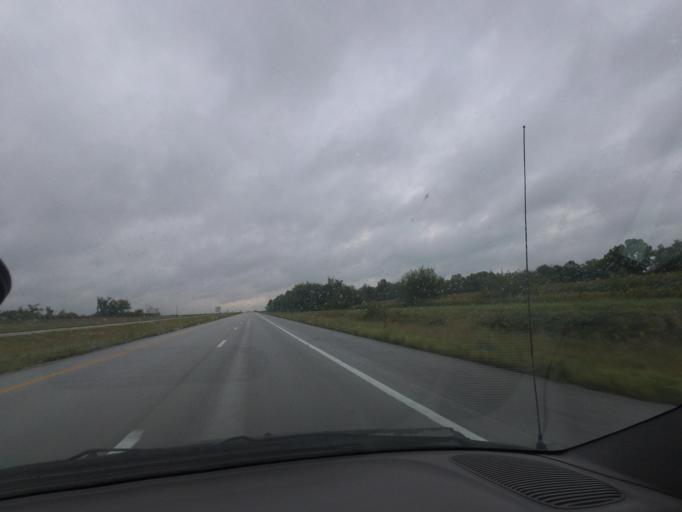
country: US
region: Missouri
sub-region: Marion County
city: Monroe City
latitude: 39.6639
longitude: -91.7014
